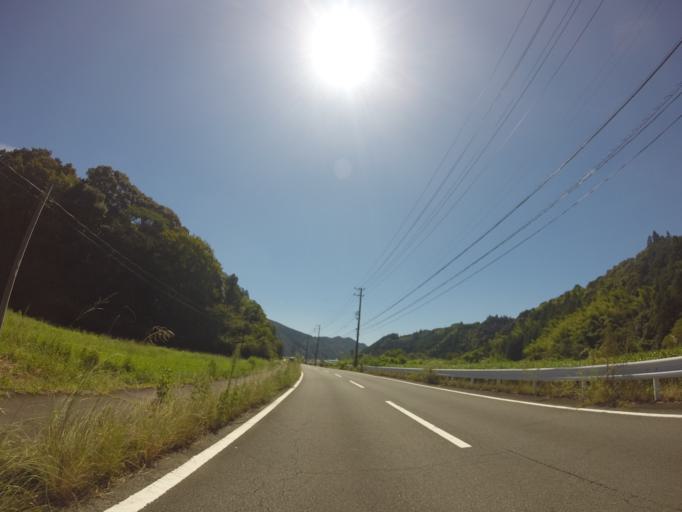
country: JP
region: Shizuoka
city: Fujieda
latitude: 34.9319
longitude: 138.2039
